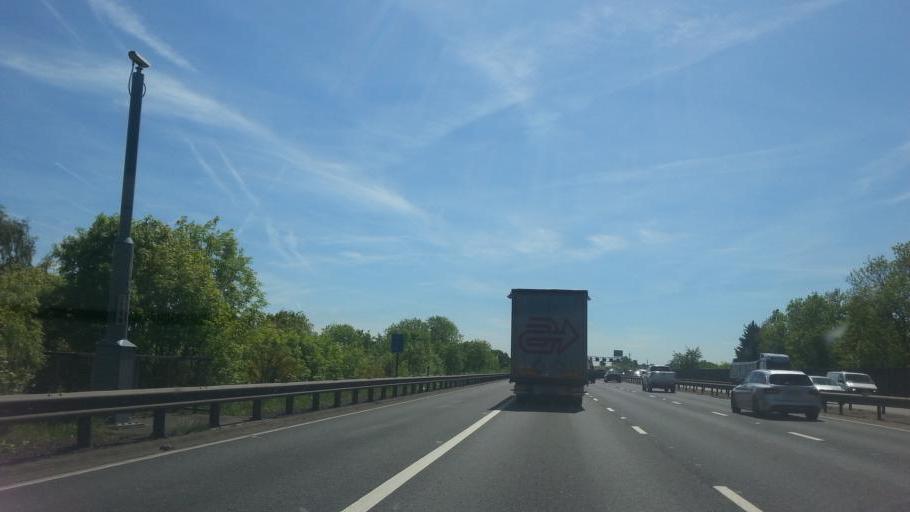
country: GB
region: England
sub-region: Central Bedfordshire
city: Steppingley
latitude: 51.9858
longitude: -0.5303
